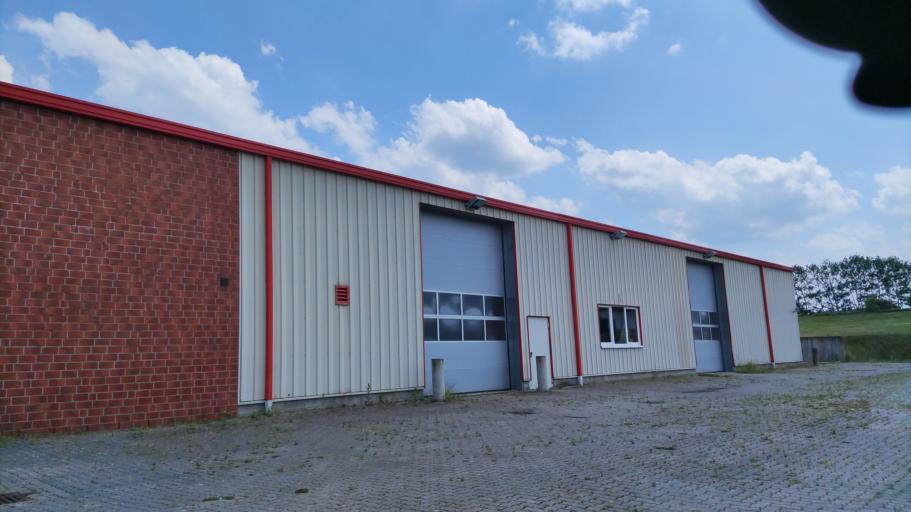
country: DE
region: Lower Saxony
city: Betzendorf
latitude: 53.1480
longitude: 10.2955
